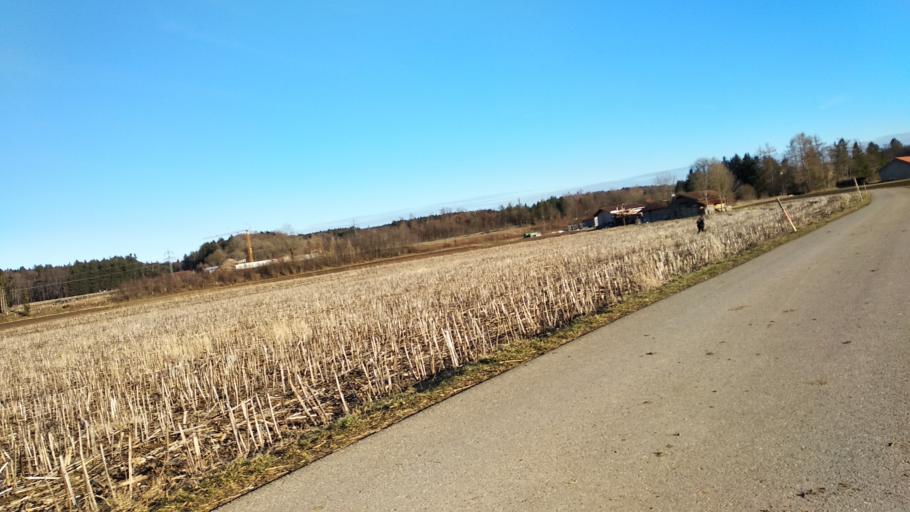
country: DE
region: Bavaria
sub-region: Upper Bavaria
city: Aying
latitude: 47.9781
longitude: 11.7740
